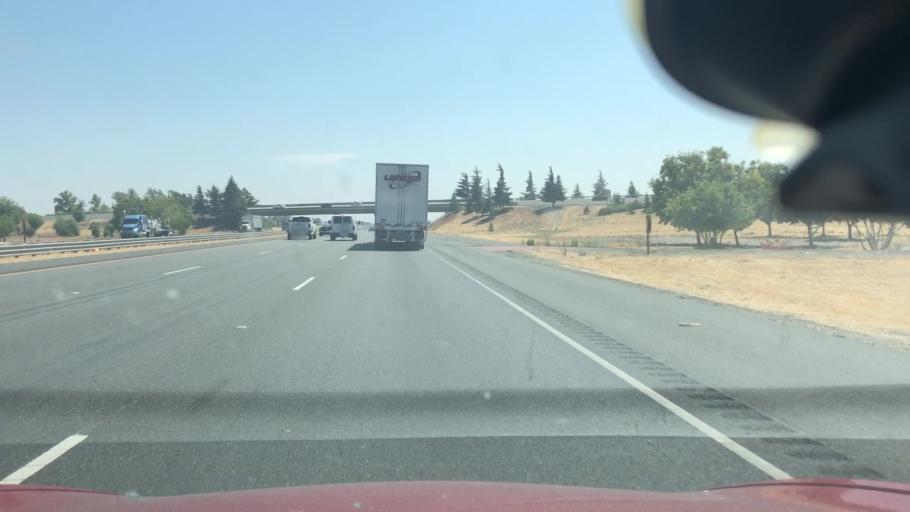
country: US
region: California
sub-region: Sacramento County
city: Laguna
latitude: 38.4291
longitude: -121.4882
